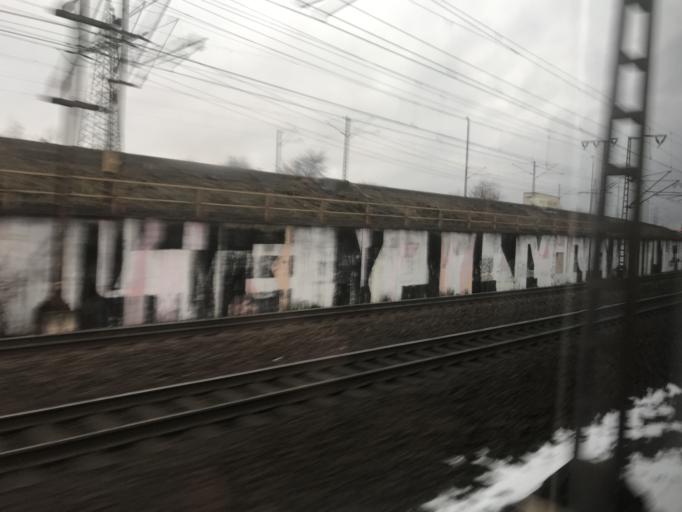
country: DE
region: Hesse
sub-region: Regierungsbezirk Kassel
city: Fulda
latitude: 50.5307
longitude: 9.6888
